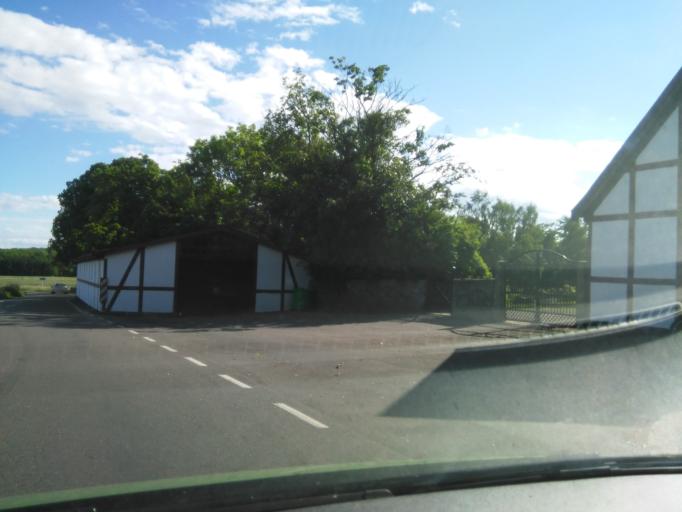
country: DK
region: Capital Region
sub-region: Bornholm Kommune
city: Akirkeby
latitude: 55.1380
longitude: 15.0172
